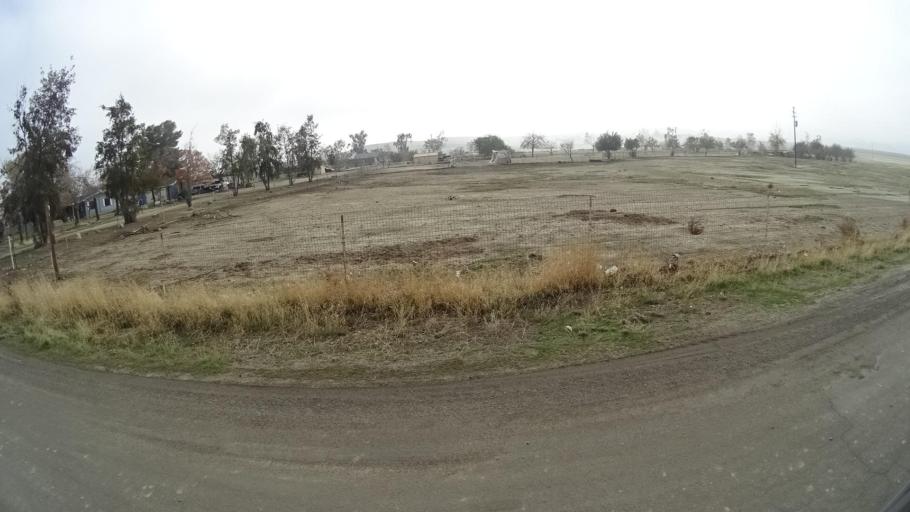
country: US
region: California
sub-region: Kern County
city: Maricopa
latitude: 35.0471
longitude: -119.3545
